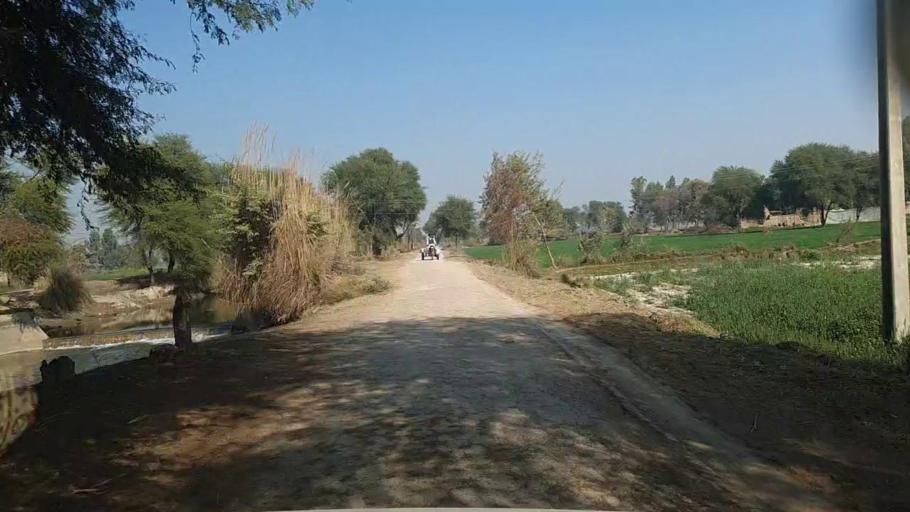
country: PK
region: Sindh
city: Khairpur
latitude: 27.9762
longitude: 69.7099
